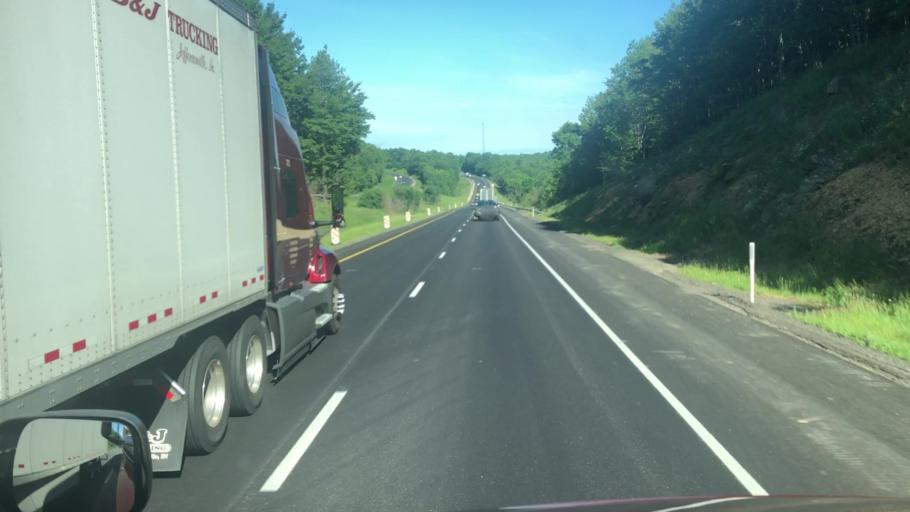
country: US
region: Pennsylvania
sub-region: Centre County
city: Milesburg
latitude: 41.0220
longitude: -77.9010
